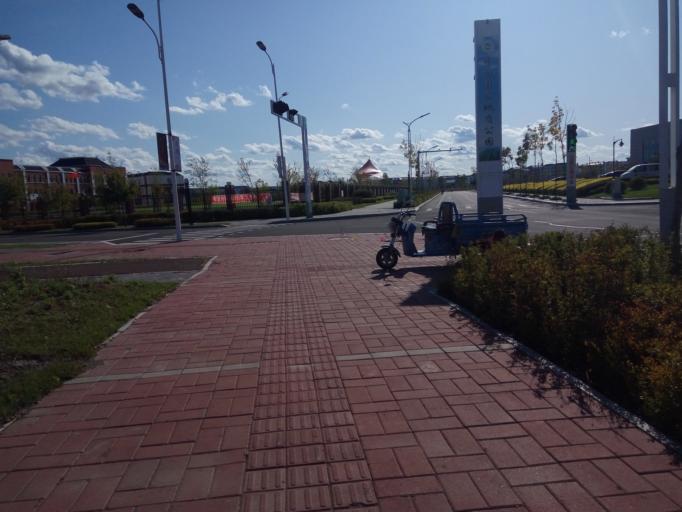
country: CN
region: Heilongjiang Sheng
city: Erjing
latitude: 48.6304
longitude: 126.1192
